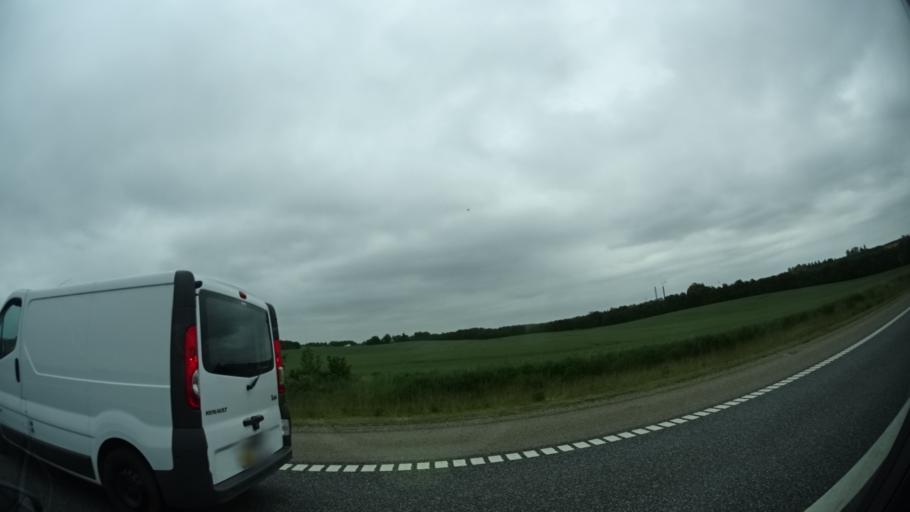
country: DK
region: Central Jutland
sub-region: Arhus Kommune
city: Trige
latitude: 56.2230
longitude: 10.1251
